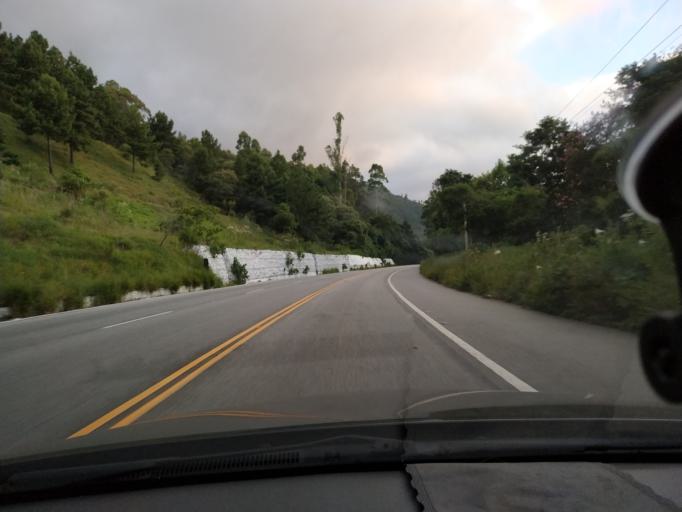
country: BR
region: Sao Paulo
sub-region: Campos Do Jordao
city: Campos do Jordao
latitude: -22.7982
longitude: -45.6259
